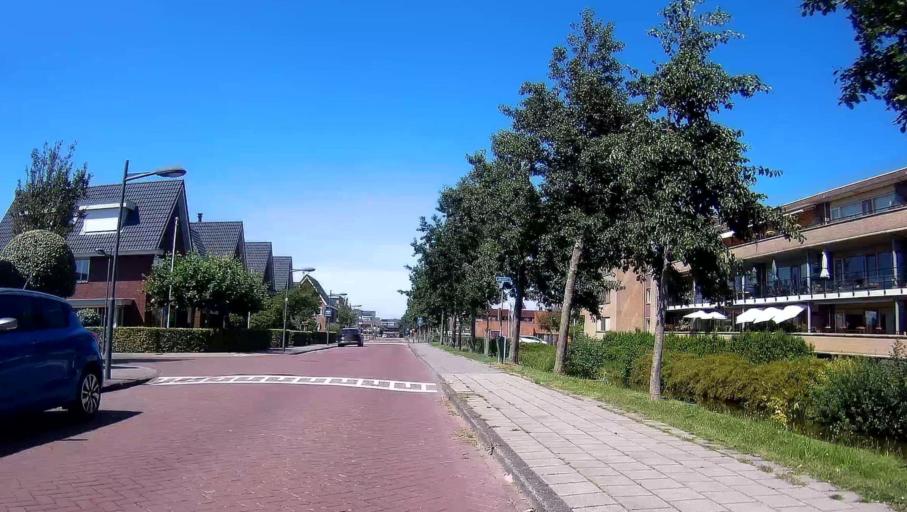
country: NL
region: South Holland
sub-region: Gemeente Westland
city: Naaldwijk
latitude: 52.0001
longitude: 4.2053
